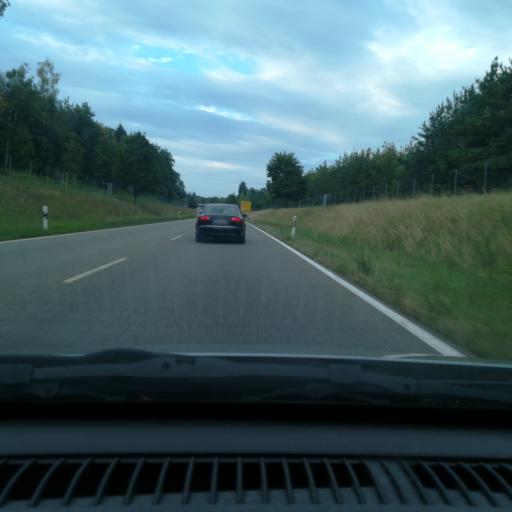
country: DE
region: Baden-Wuerttemberg
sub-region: Freiburg Region
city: Moos
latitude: 47.7653
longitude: 8.9109
